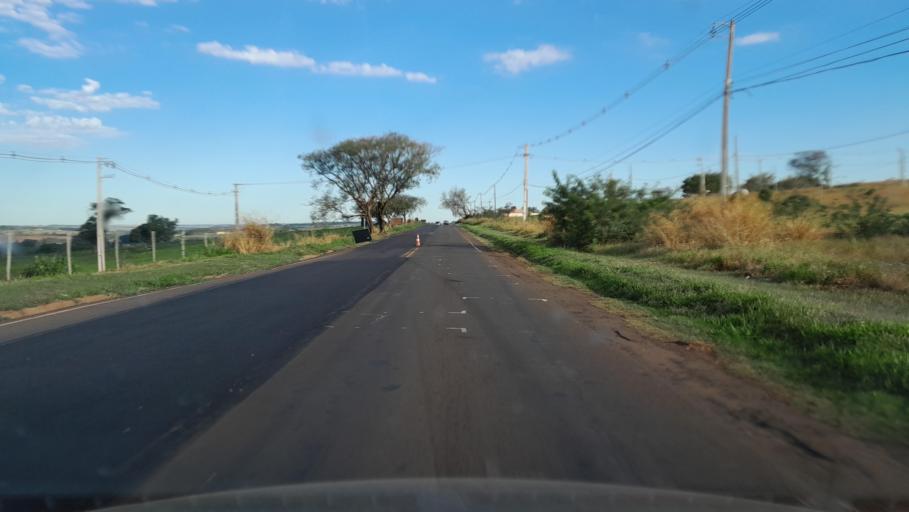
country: BR
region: Parana
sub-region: Umuarama
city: Umuarama
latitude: -23.7647
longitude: -53.2702
